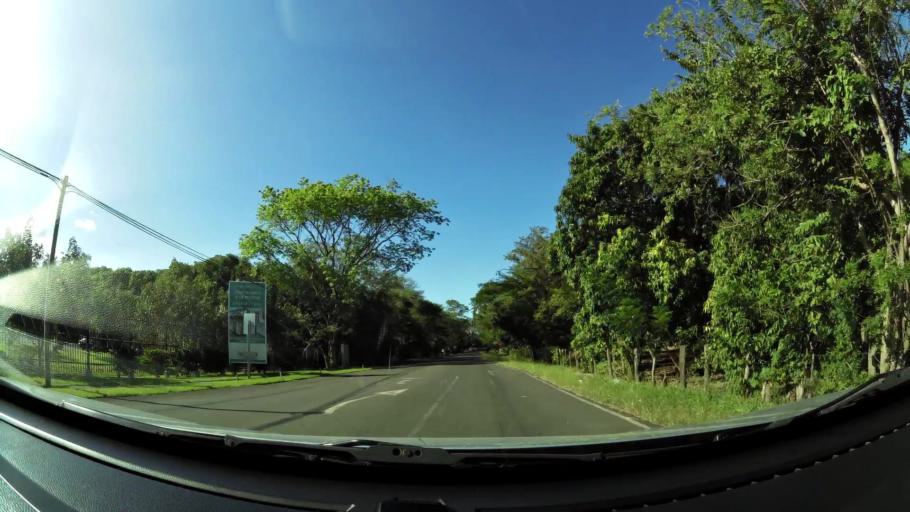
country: CR
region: Guanacaste
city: Sardinal
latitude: 10.5592
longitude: -85.5941
